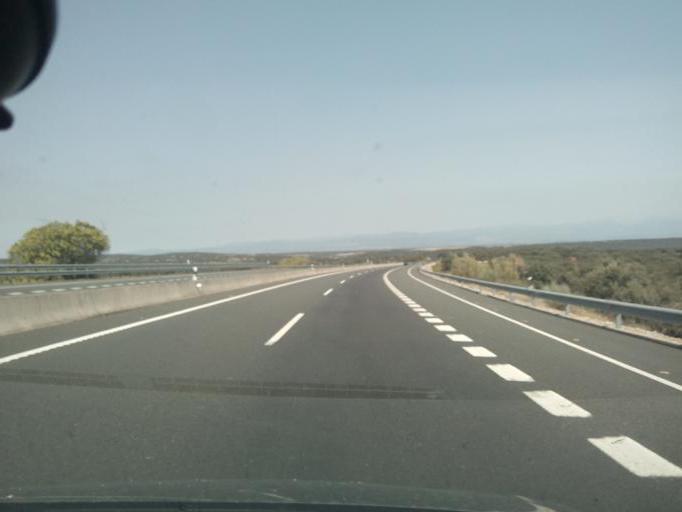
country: ES
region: Extremadura
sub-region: Provincia de Caceres
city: Casas de Miravete
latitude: 39.7598
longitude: -5.7321
